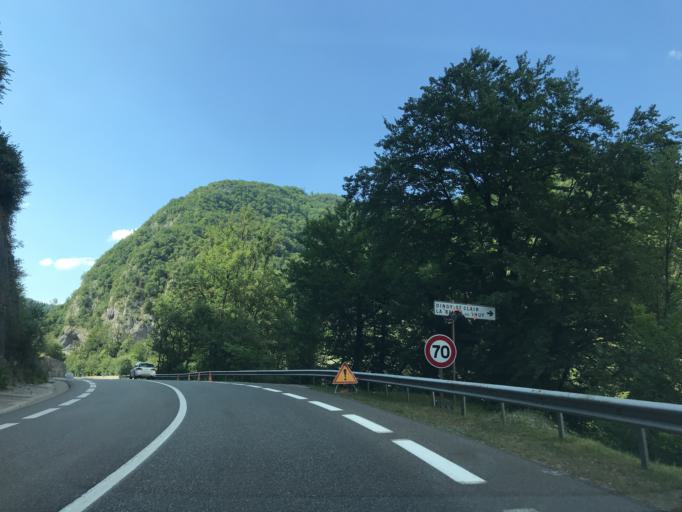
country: FR
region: Rhone-Alpes
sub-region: Departement de la Haute-Savoie
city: Dingy-Saint-Clair
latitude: 45.9017
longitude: 6.2114
